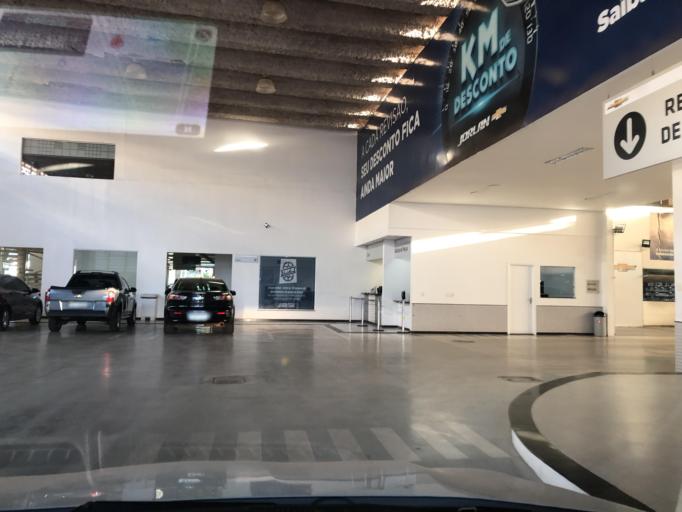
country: BR
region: Federal District
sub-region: Brasilia
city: Brasilia
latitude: -15.8026
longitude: -47.9618
